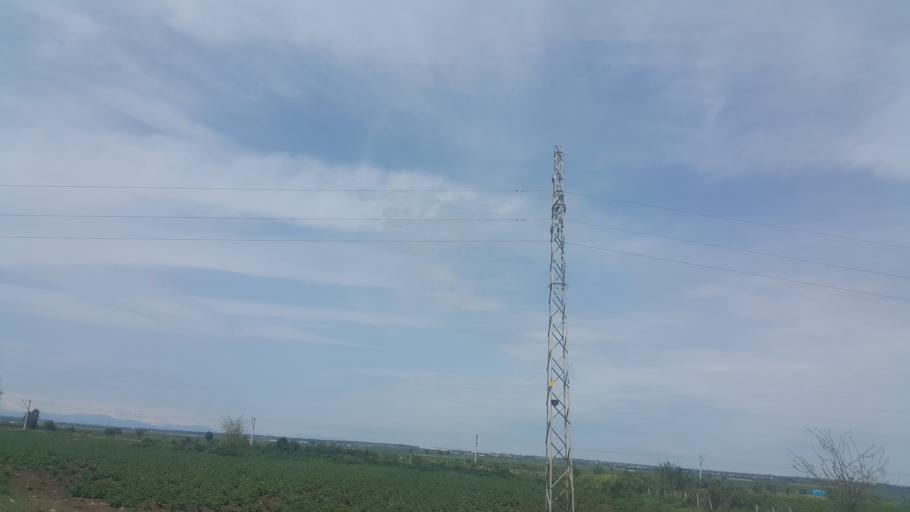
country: TR
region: Adana
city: Yuregir
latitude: 36.9772
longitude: 35.4746
